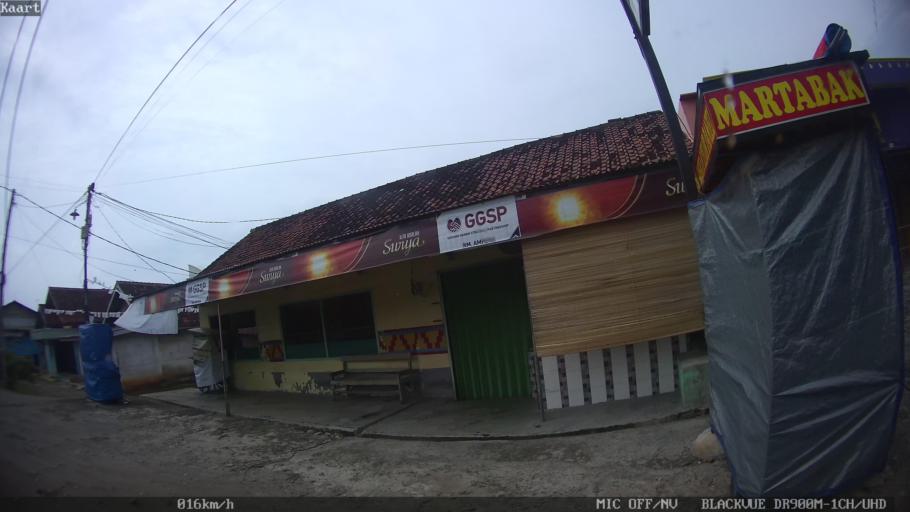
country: ID
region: Lampung
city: Kedaton
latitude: -5.3918
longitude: 105.2131
